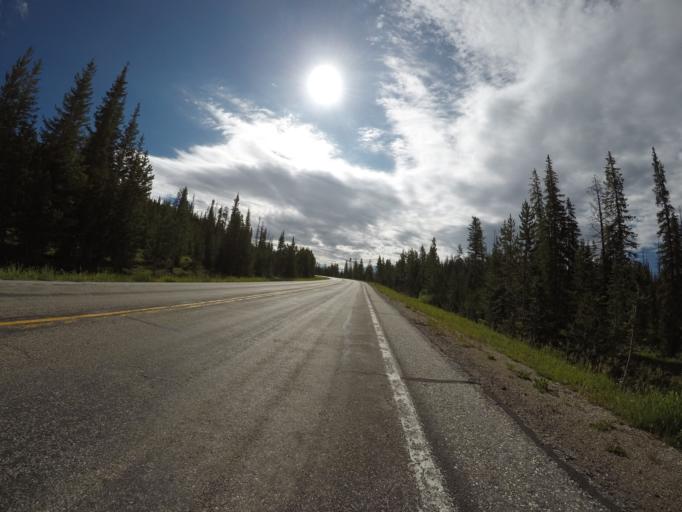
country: US
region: Wyoming
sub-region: Carbon County
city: Saratoga
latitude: 41.3264
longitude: -106.4375
